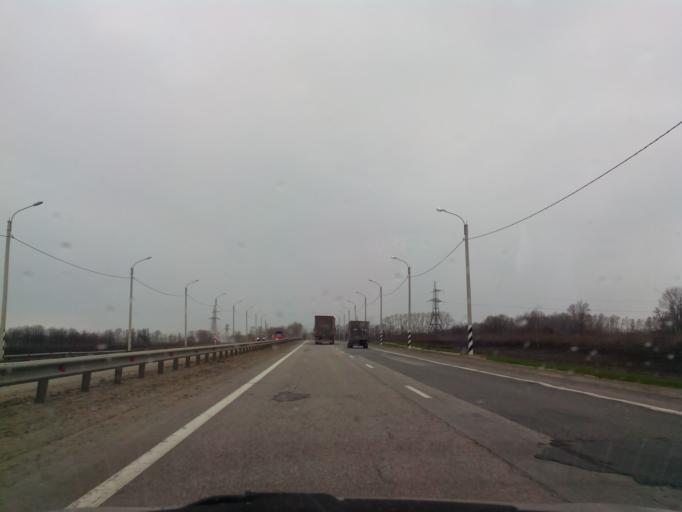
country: RU
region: Tambov
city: Selezni
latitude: 52.7500
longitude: 41.1841
